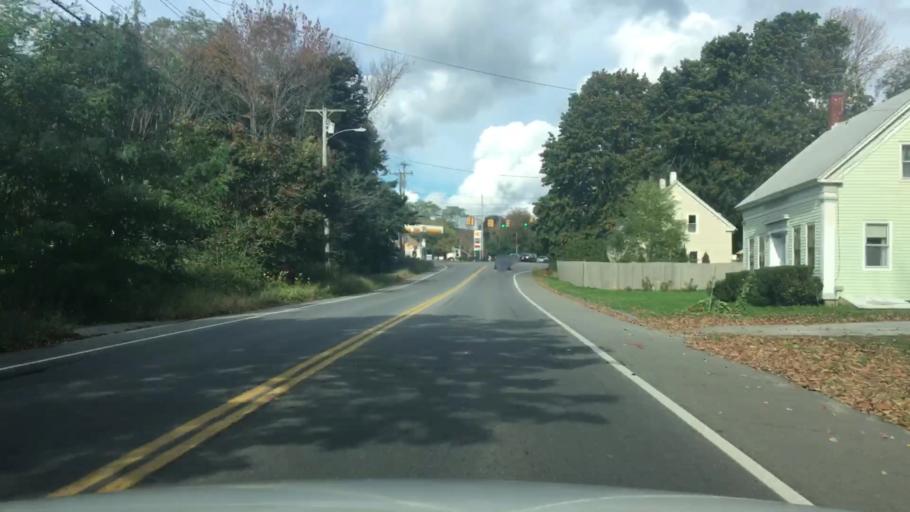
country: US
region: Maine
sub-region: Knox County
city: Rockland
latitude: 44.1228
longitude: -69.1163
